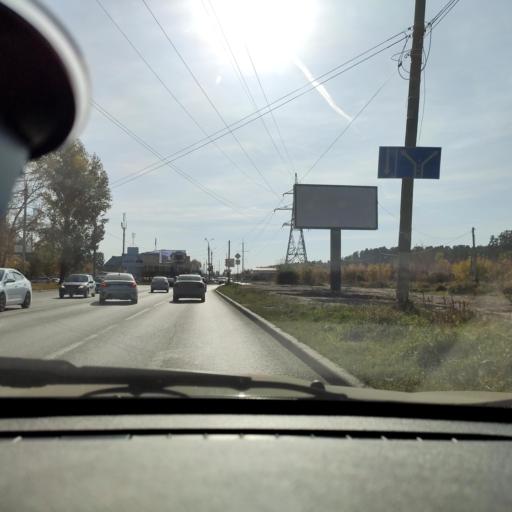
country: RU
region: Samara
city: Tol'yatti
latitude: 53.5254
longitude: 49.3962
